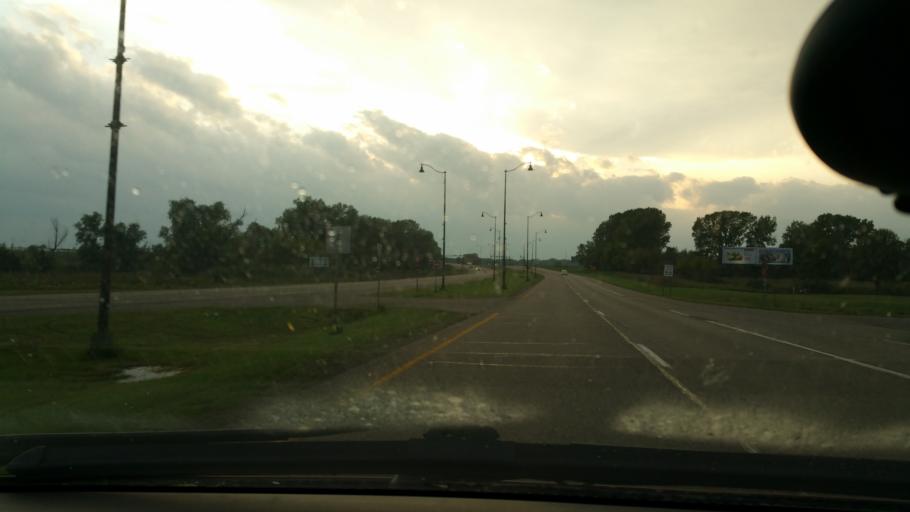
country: US
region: Minnesota
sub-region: Freeborn County
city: Albert Lea
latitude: 43.6594
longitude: -93.3228
